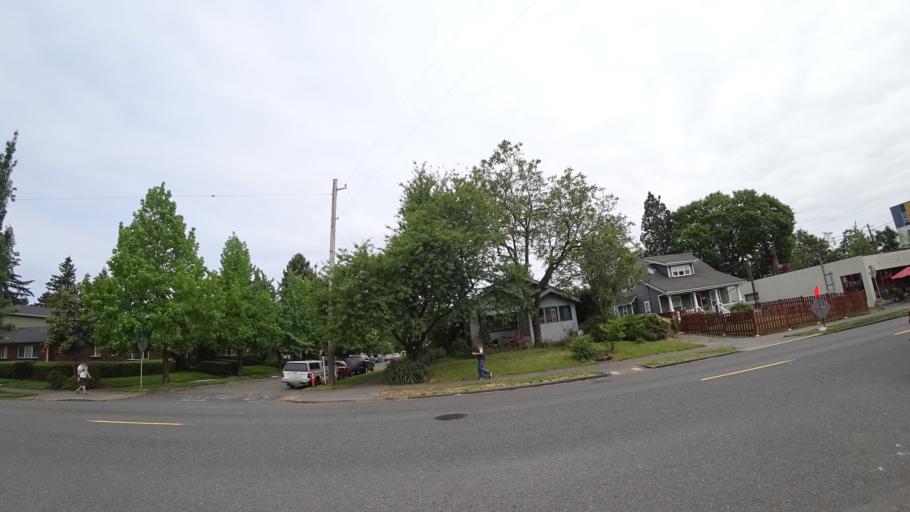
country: US
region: Oregon
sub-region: Multnomah County
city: Portland
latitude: 45.5626
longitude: -122.6359
